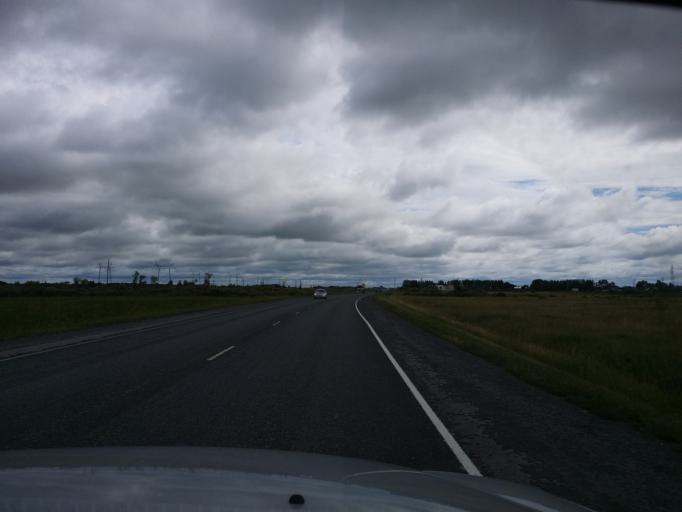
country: RU
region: Tjumen
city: Yarkovo
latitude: 57.1763
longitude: 66.5692
